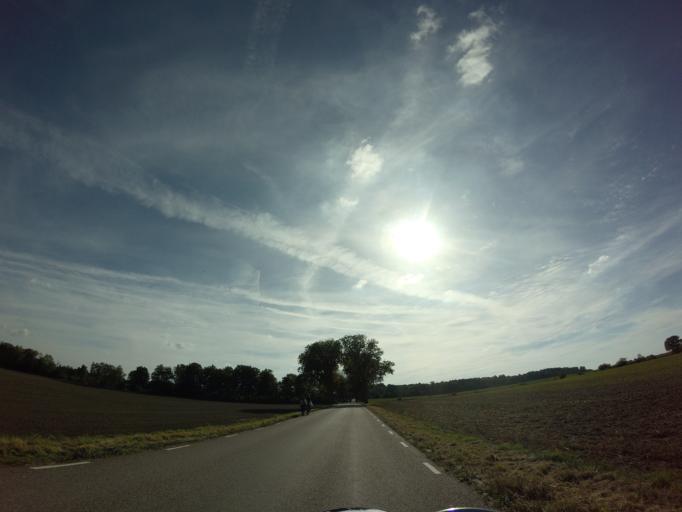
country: SE
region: Skane
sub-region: Lunds Kommun
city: Genarp
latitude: 55.6046
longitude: 13.3661
